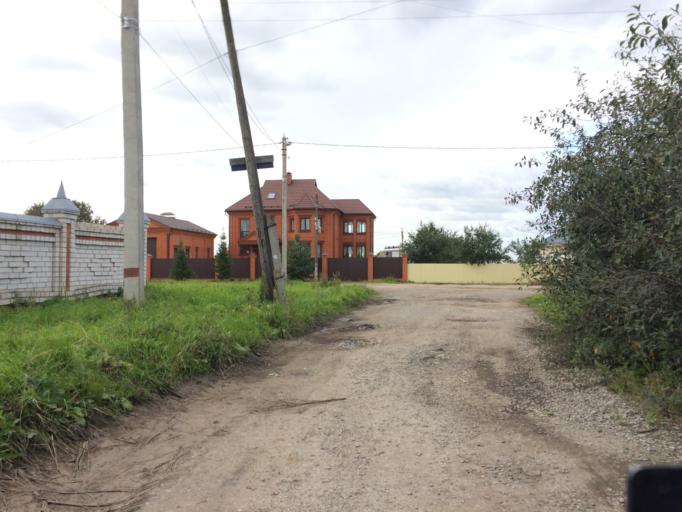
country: RU
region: Mariy-El
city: Yoshkar-Ola
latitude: 56.6626
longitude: 47.9923
